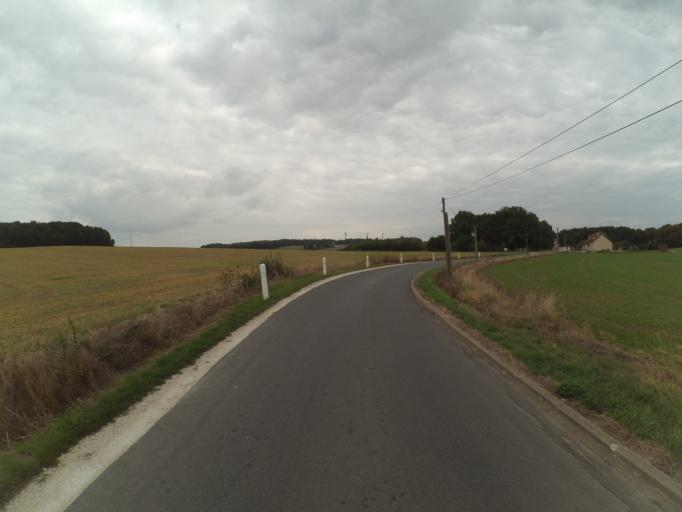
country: FR
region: Centre
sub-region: Departement d'Indre-et-Loire
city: Auzouer-en-Touraine
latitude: 47.5057
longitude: 0.9243
